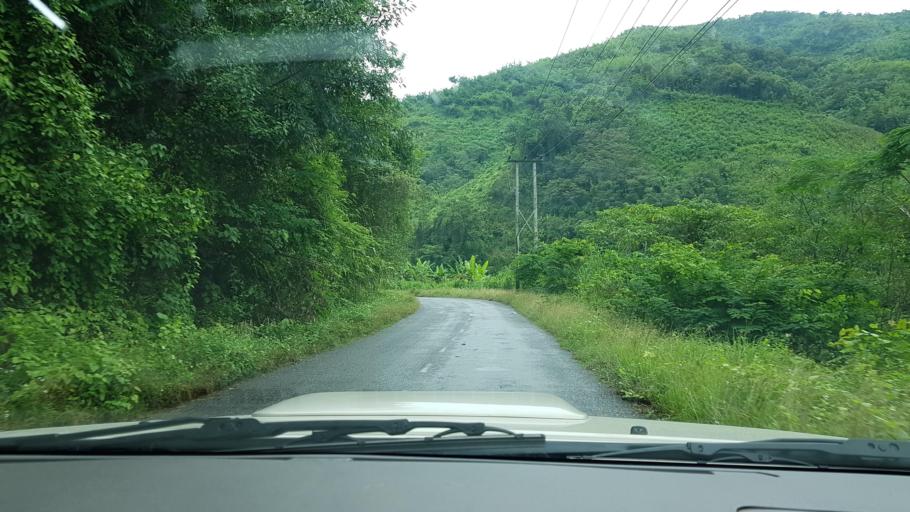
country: LA
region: Phongsali
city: Khoa
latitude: 21.1018
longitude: 102.2795
